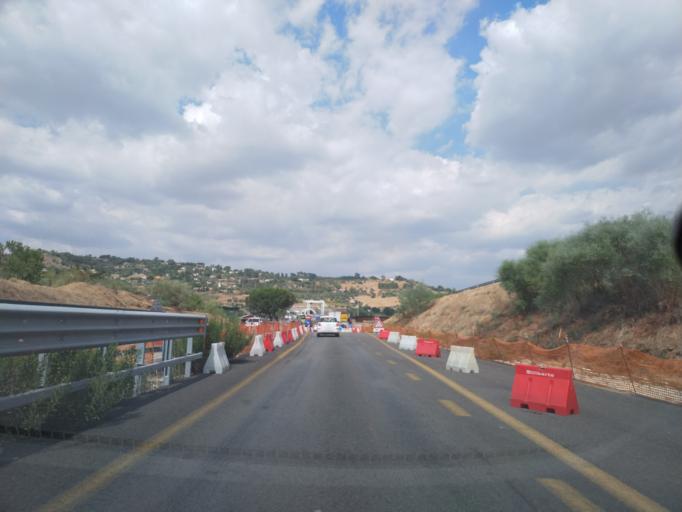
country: IT
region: Sicily
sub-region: Provincia di Caltanissetta
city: San Cataldo
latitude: 37.4712
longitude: 14.0109
